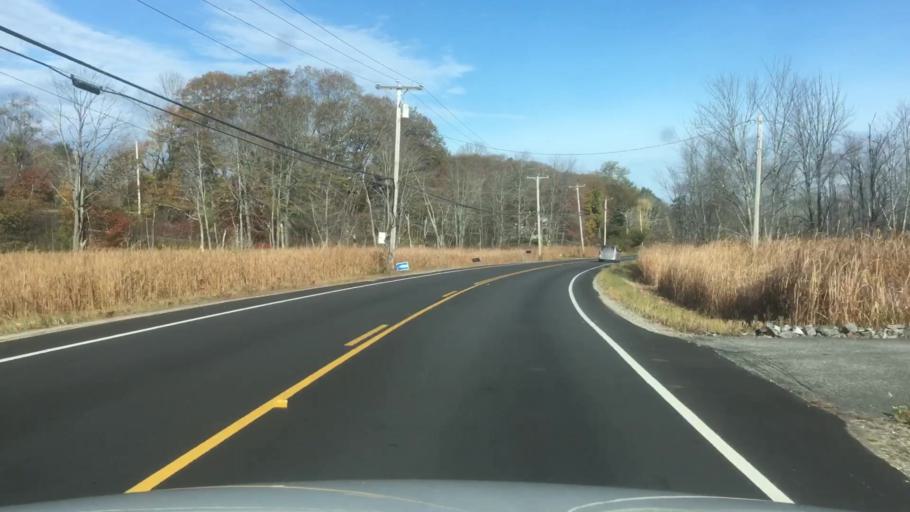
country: US
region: Maine
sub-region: Sagadahoc County
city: Woolwich
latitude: 43.9035
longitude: -69.7974
